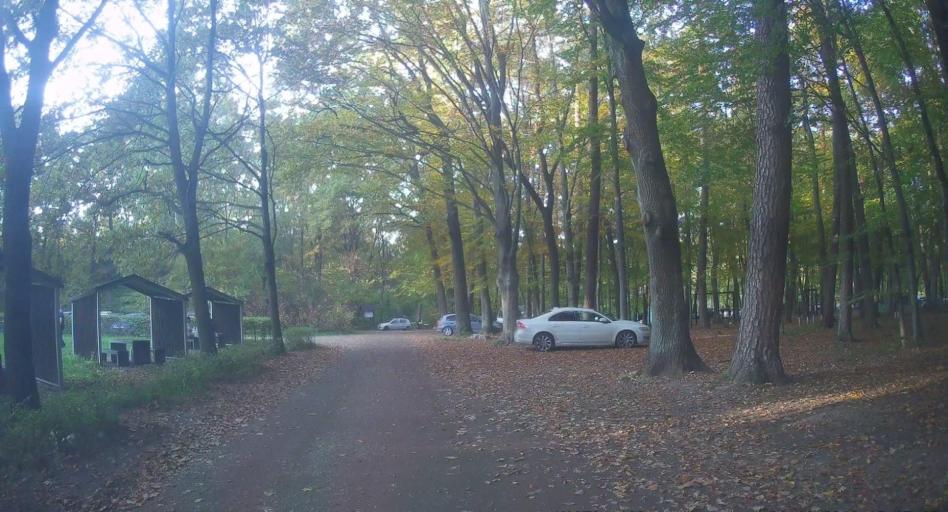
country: PL
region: Lesser Poland Voivodeship
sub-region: Powiat wielicki
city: Niepolomice
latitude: 50.0143
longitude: 20.2407
